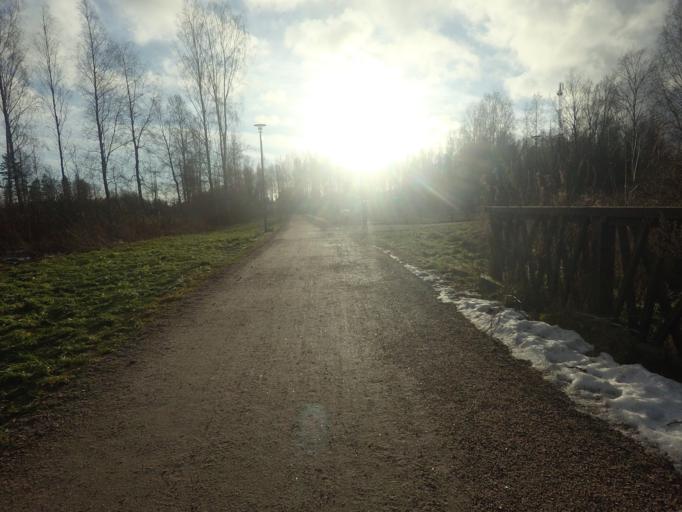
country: FI
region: Uusimaa
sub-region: Helsinki
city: Kilo
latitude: 60.1993
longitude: 24.7735
